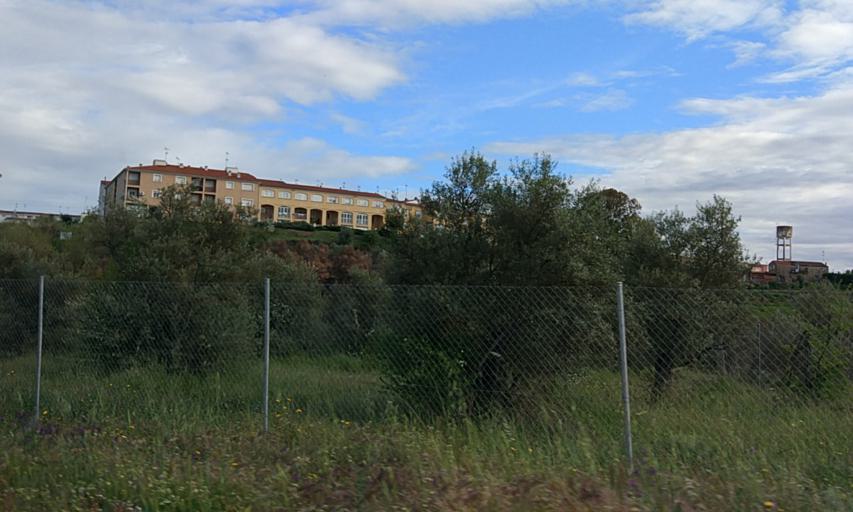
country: ES
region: Extremadura
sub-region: Provincia de Caceres
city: Coria
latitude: 39.9962
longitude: -6.5433
